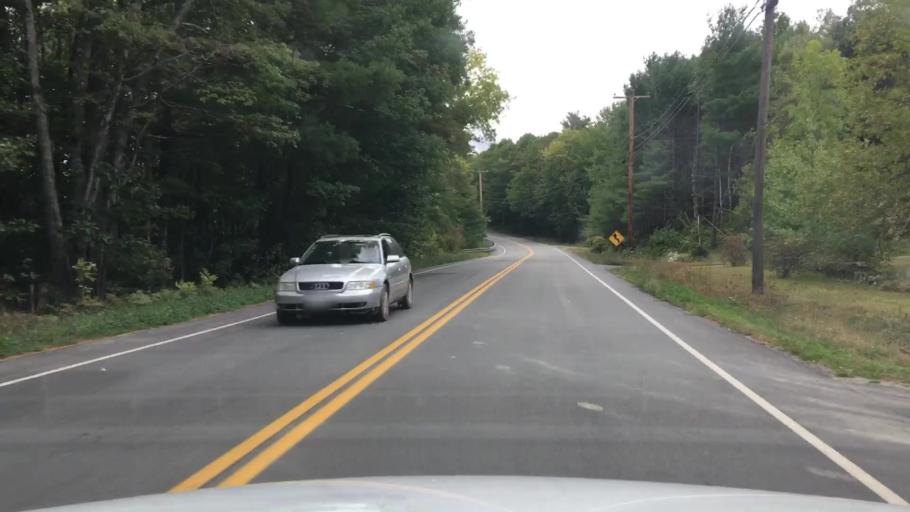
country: US
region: Maine
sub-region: Penobscot County
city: Milford
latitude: 44.9584
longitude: -68.6975
